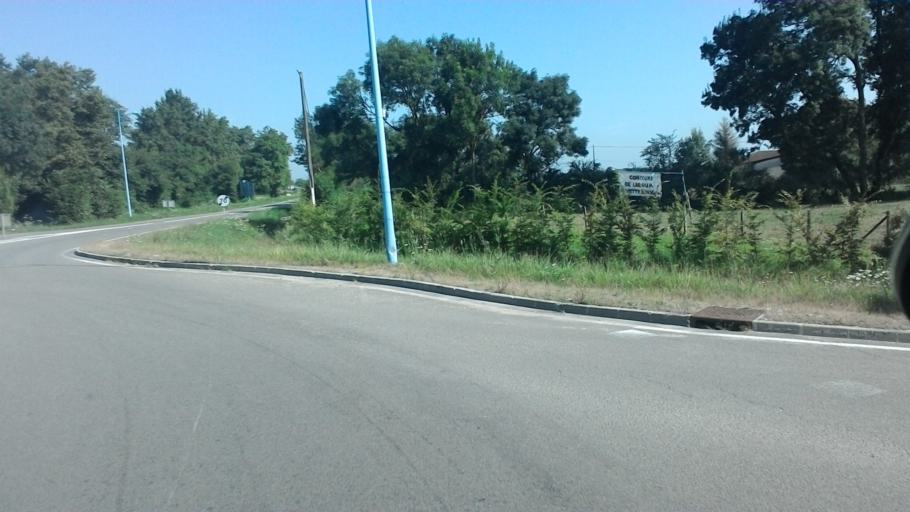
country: FR
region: Rhone-Alpes
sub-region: Departement de l'Ain
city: Montrevel-en-Bresse
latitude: 46.3482
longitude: 5.1260
